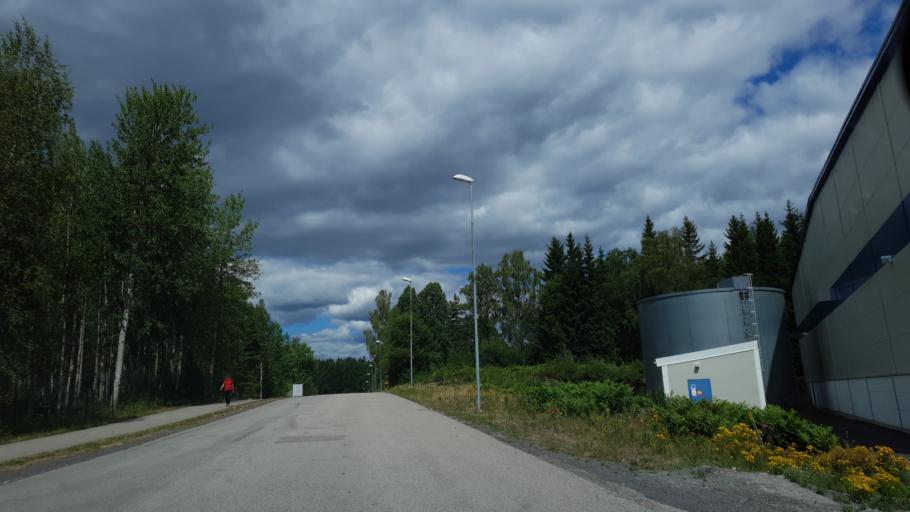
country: SE
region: Kronoberg
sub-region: Uppvidinge Kommun
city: Aseda
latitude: 57.1696
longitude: 15.3711
